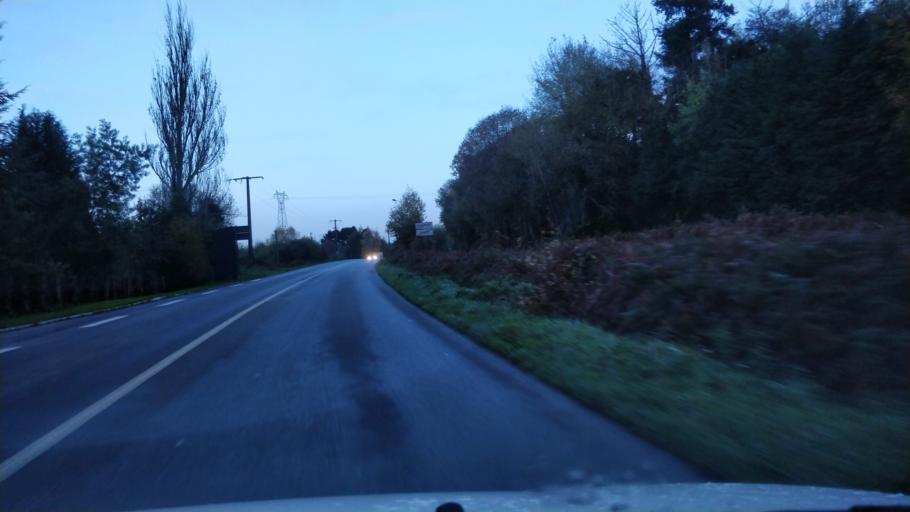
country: FR
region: Brittany
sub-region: Departement du Morbihan
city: Pontivy
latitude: 48.0811
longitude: -2.9485
